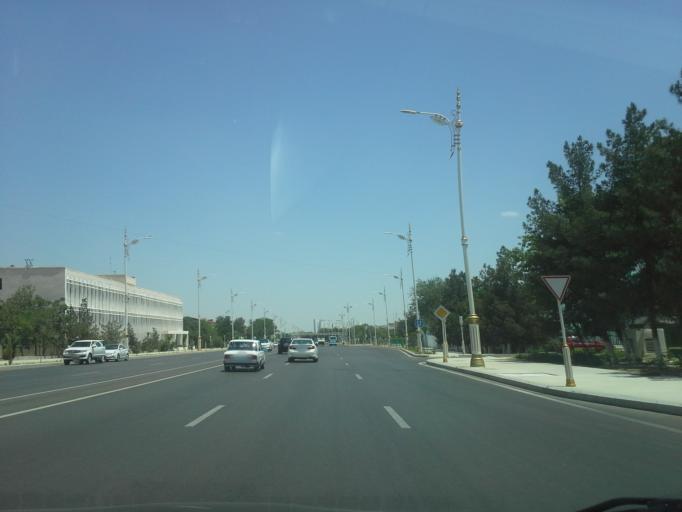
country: TM
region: Ahal
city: Ashgabat
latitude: 37.9205
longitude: 58.3957
